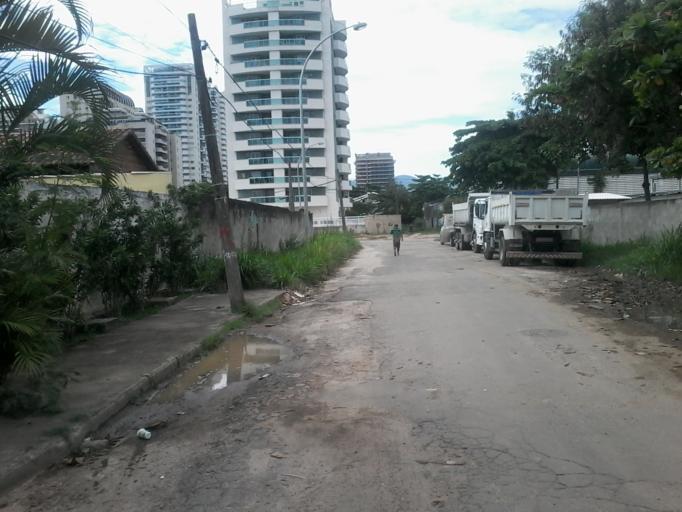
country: BR
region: Rio de Janeiro
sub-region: Nilopolis
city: Nilopolis
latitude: -23.0247
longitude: -43.4845
